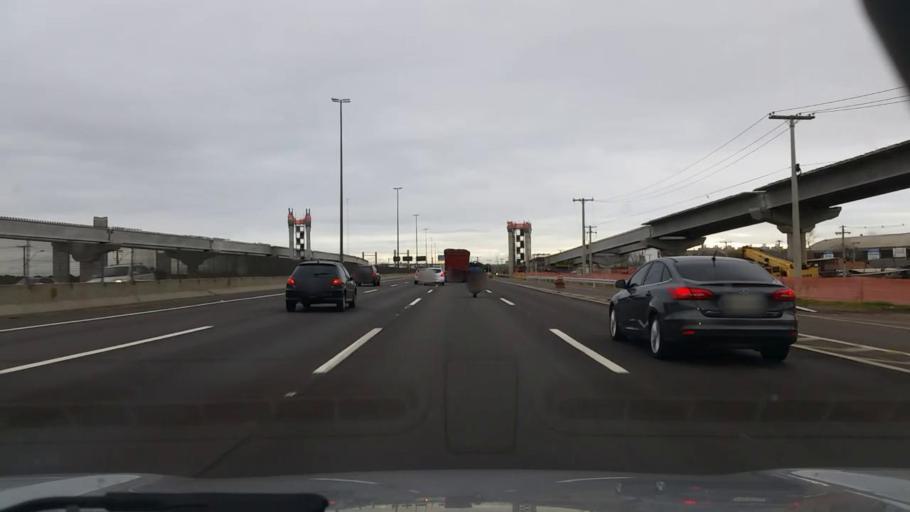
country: BR
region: Rio Grande do Sul
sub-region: Porto Alegre
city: Porto Alegre
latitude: -29.9880
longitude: -51.2032
